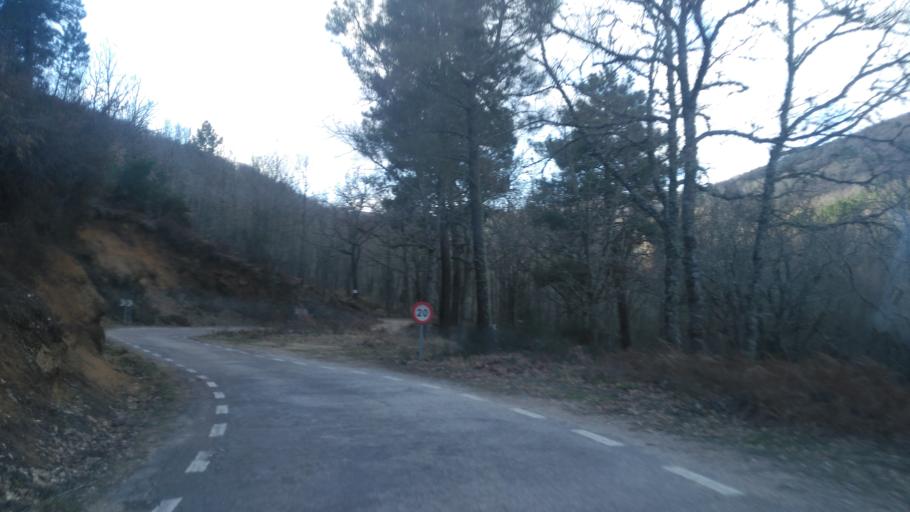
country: ES
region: Castille and Leon
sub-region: Provincia de Salamanca
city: Mogarraz
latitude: 40.5056
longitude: -6.0479
